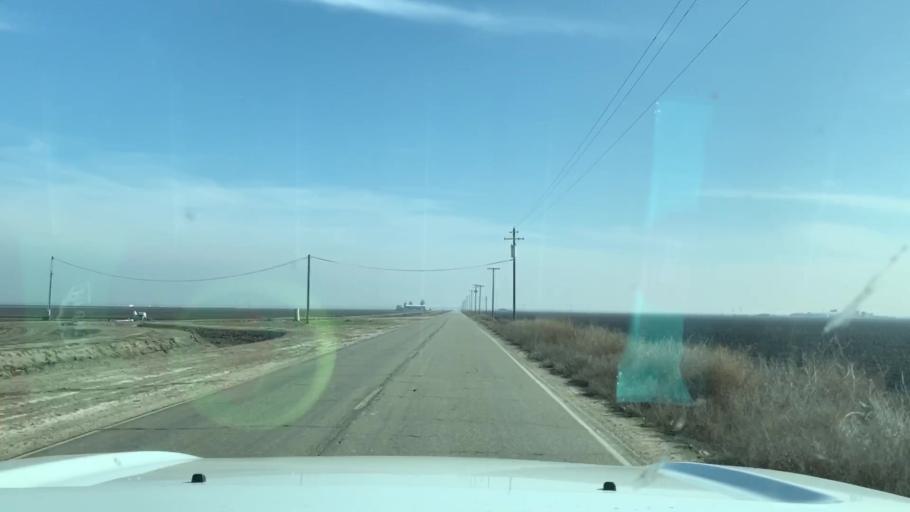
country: US
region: California
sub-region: Kern County
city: Buttonwillow
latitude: 35.4420
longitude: -119.5297
